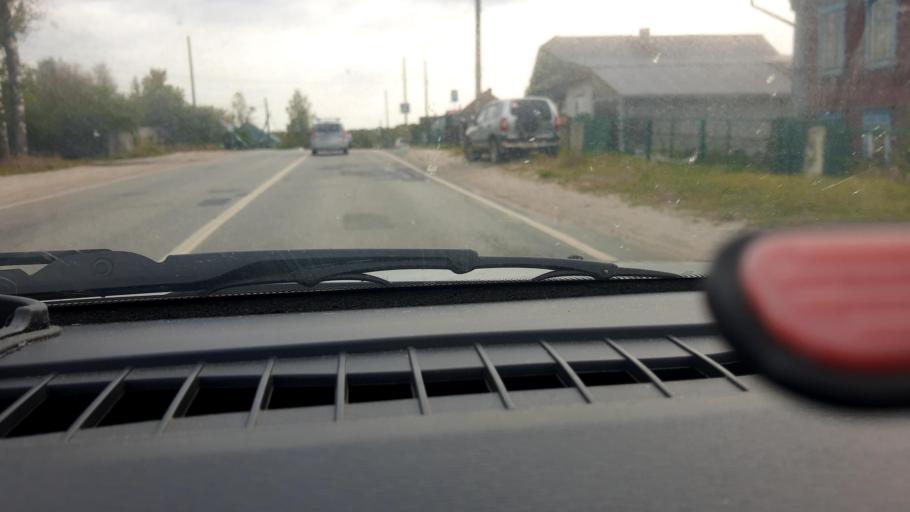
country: RU
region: Nizjnij Novgorod
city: Krasnyye Baki
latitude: 57.0672
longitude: 45.1372
